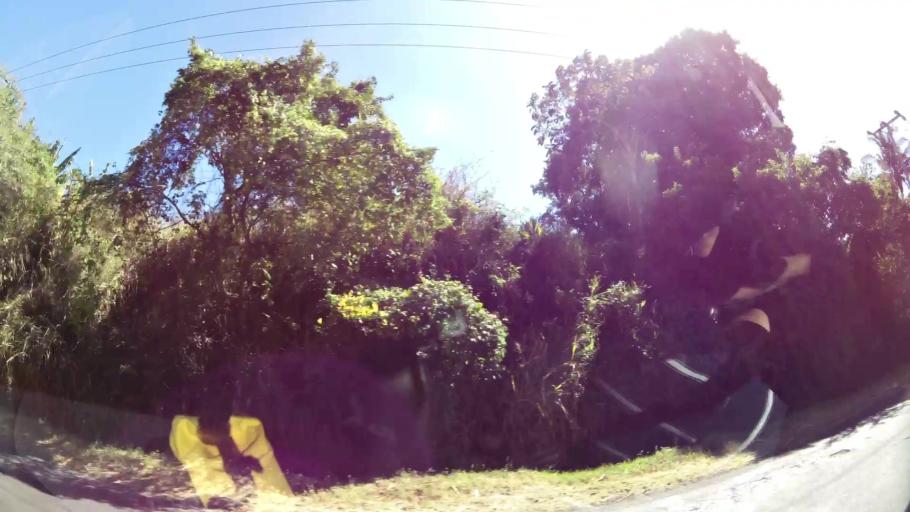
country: SV
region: La Libertad
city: San Juan Opico
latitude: 13.8628
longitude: -89.3591
